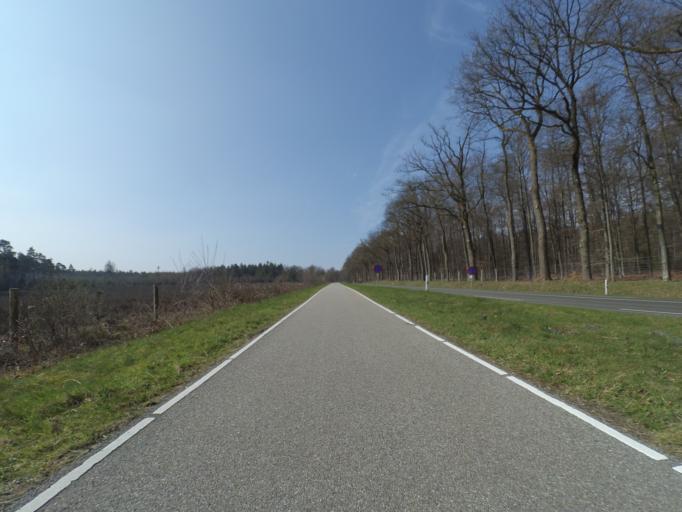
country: NL
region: Gelderland
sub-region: Gemeente Apeldoorn
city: Beekbergen
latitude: 52.1627
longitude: 5.8988
